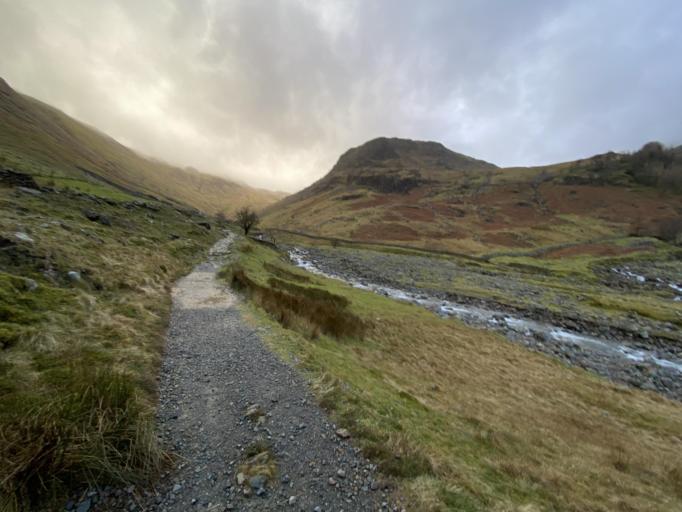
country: GB
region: England
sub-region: Cumbria
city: Keswick
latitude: 54.4897
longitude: -3.1828
